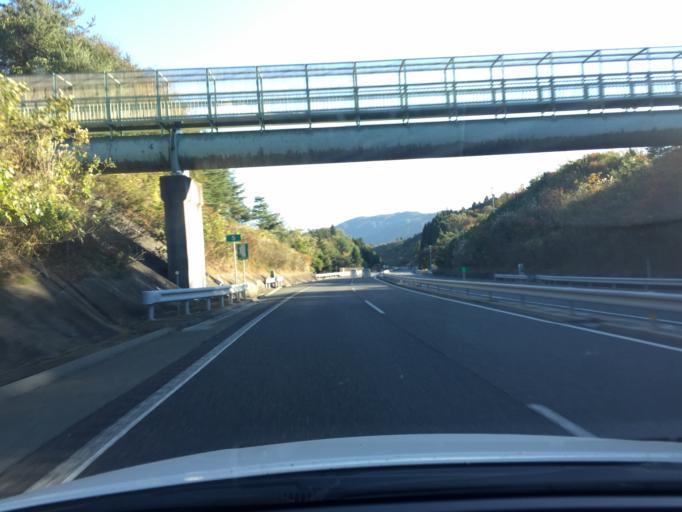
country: JP
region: Fukushima
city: Iwaki
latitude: 37.0765
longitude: 140.7912
